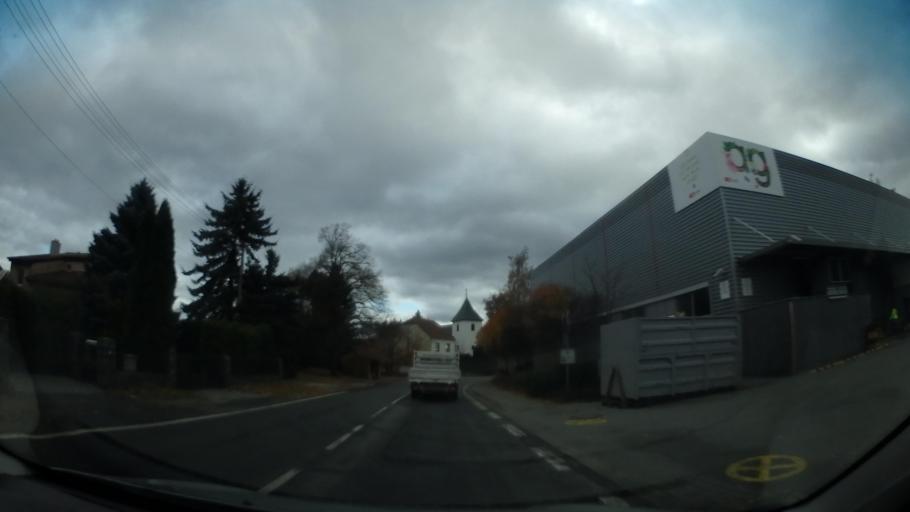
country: CZ
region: Vysocina
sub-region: Okres Zd'ar nad Sazavou
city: Velka Bites
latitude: 49.2698
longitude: 16.2380
